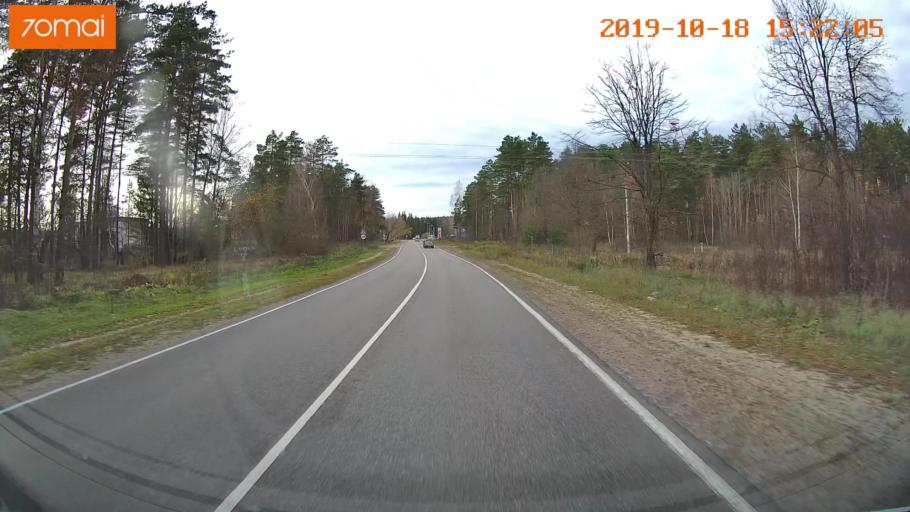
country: RU
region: Vladimir
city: Anopino
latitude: 55.7055
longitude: 40.7383
